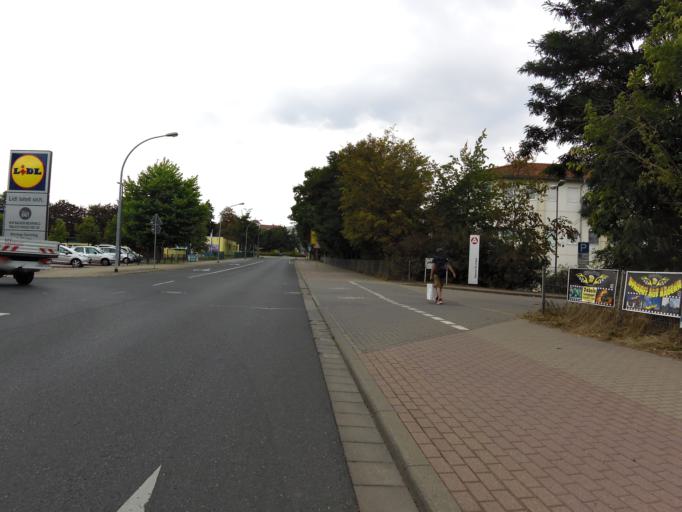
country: DE
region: Saxony
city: Dobeln
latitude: 51.1229
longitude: 13.1080
